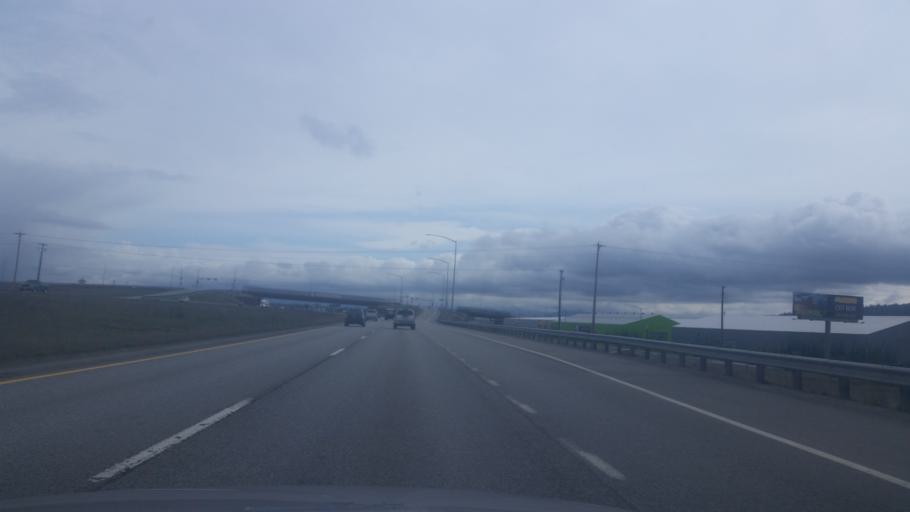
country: US
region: Washington
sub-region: Spokane County
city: Otis Orchards-East Farms
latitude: 47.6994
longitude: -117.0252
